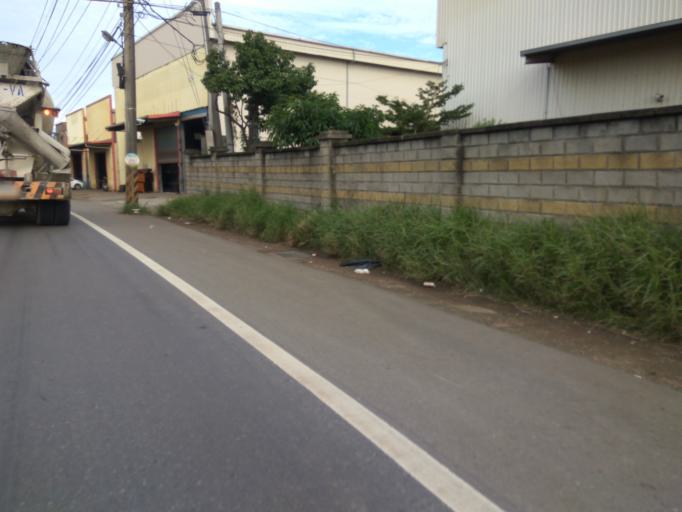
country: TW
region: Taiwan
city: Daxi
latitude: 24.9410
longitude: 121.1584
